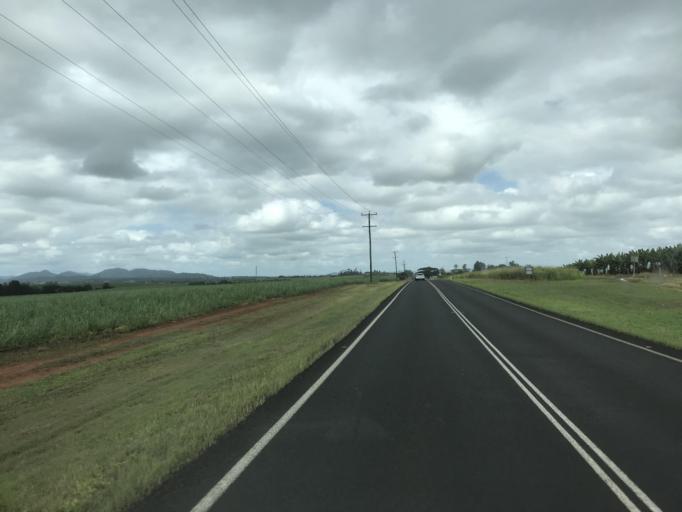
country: AU
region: Queensland
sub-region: Cassowary Coast
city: Innisfail
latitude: -17.5803
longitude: 145.9996
